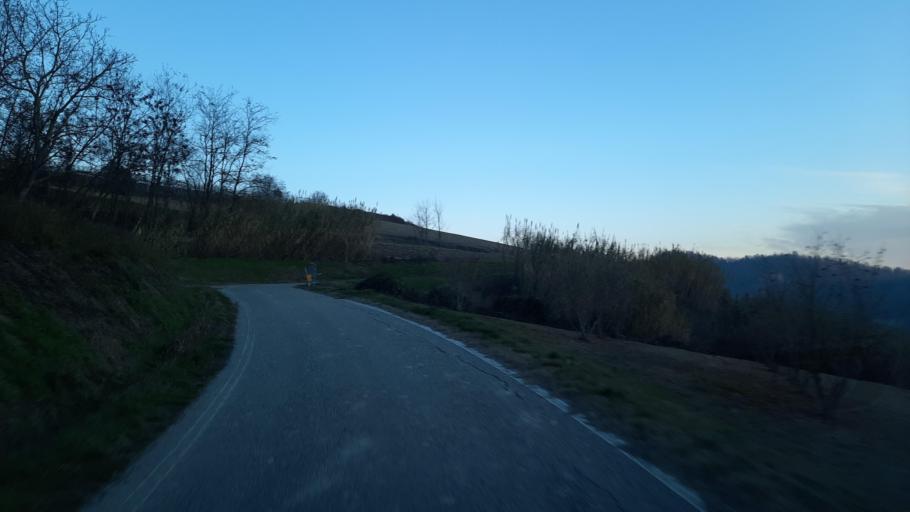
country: IT
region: Piedmont
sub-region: Provincia di Alessandria
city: Camino
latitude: 45.1547
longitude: 8.2826
